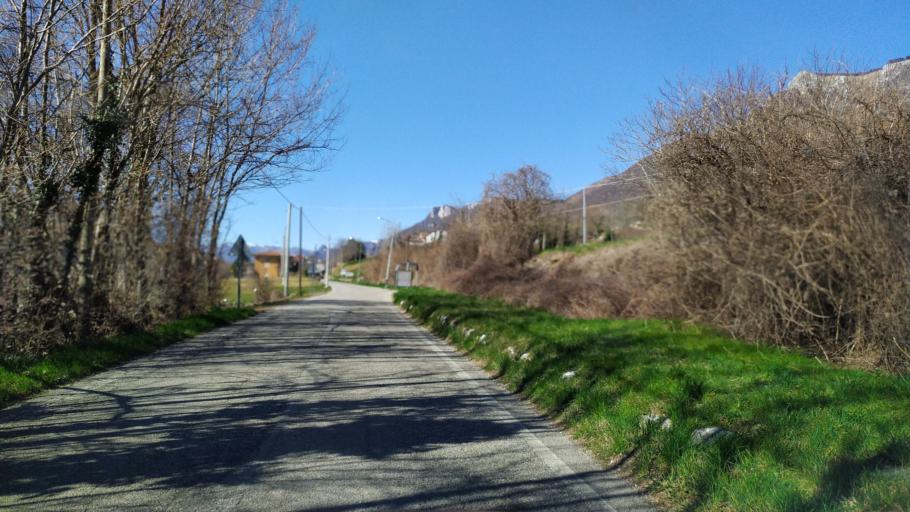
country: IT
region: Veneto
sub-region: Provincia di Vicenza
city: Chiuppano
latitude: 45.7663
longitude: 11.4726
